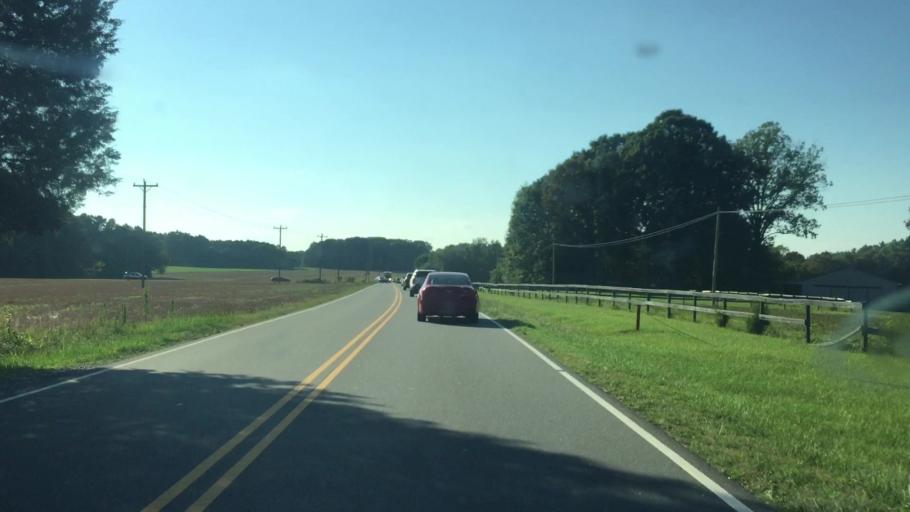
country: US
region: North Carolina
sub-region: Gaston County
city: Davidson
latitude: 35.4754
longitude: -80.7482
